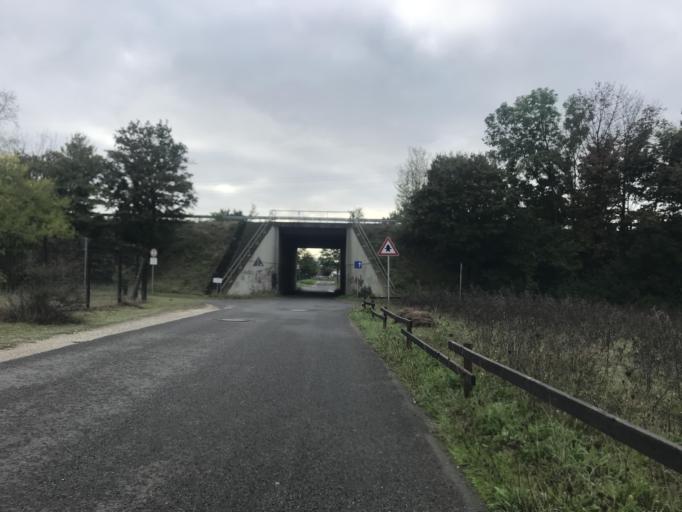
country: DE
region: Rheinland-Pfalz
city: Ingelheim am Rhein
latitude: 49.9836
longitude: 8.0401
